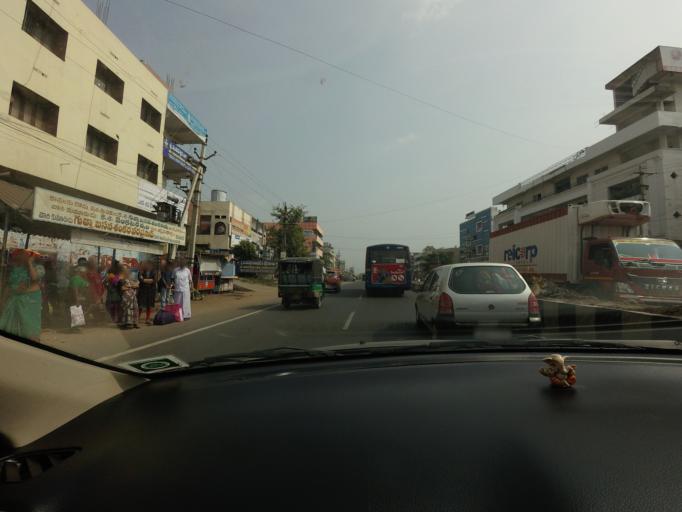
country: IN
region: Andhra Pradesh
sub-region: Krishna
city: Yanamalakuduru
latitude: 16.4838
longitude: 80.6862
